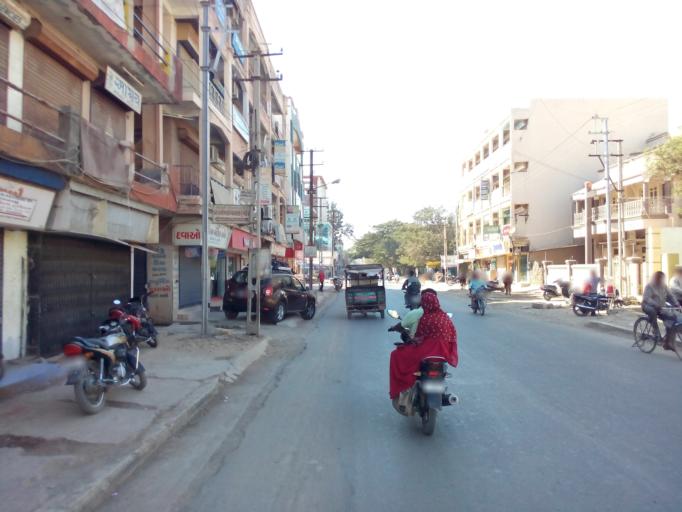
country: IN
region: Gujarat
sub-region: Porbandar
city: Porbandar
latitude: 21.6389
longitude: 69.6166
